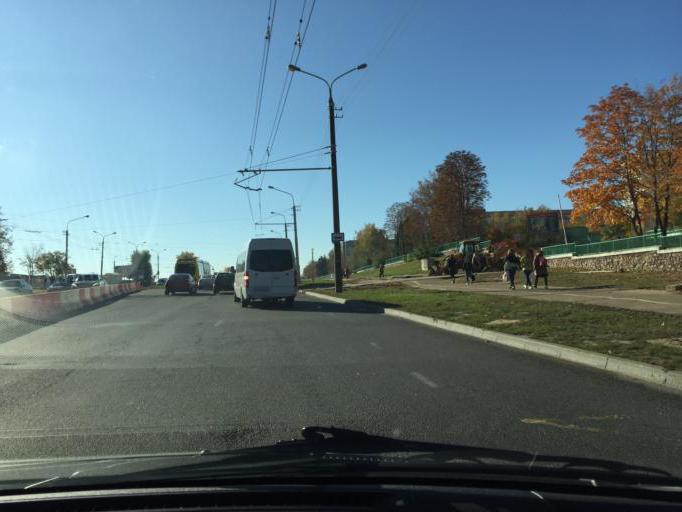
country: BY
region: Minsk
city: Syenitsa
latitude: 53.8520
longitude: 27.5373
